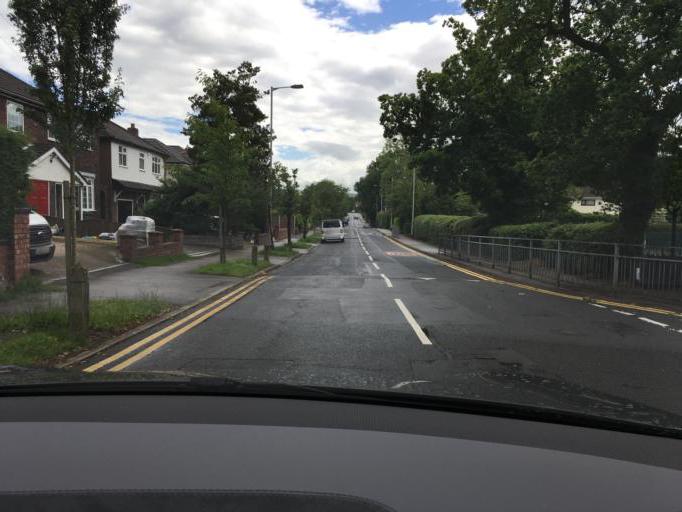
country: GB
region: England
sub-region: Borough of Stockport
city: Marple
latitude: 53.3671
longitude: -2.0680
